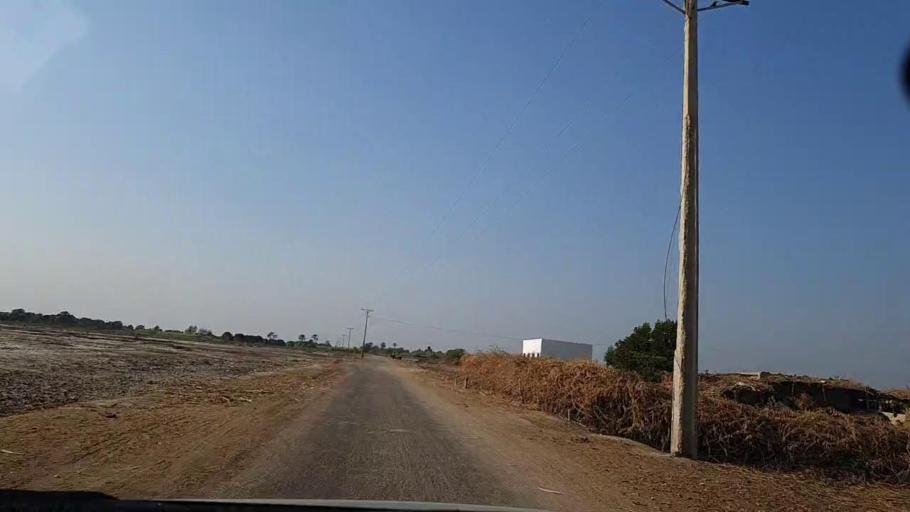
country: PK
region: Sindh
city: Mirwah Gorchani
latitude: 25.2169
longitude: 68.9932
